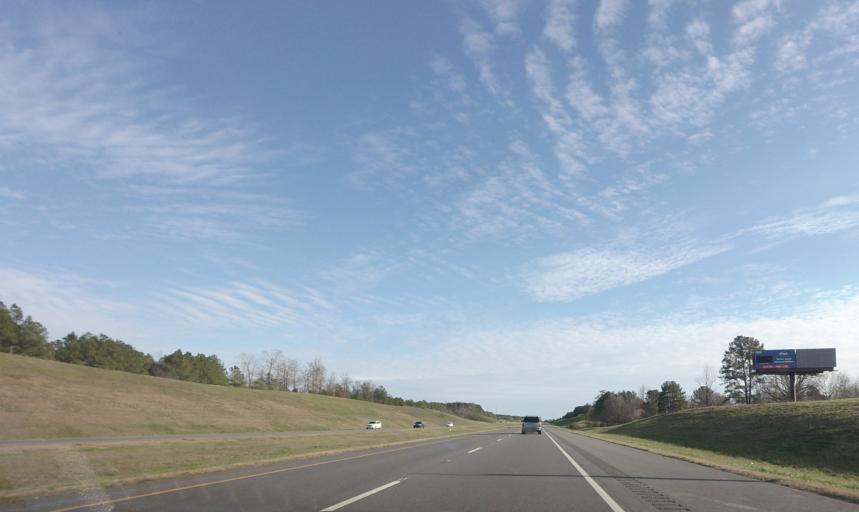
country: US
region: Alabama
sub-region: Walker County
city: Jasper
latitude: 33.8380
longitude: -87.3289
